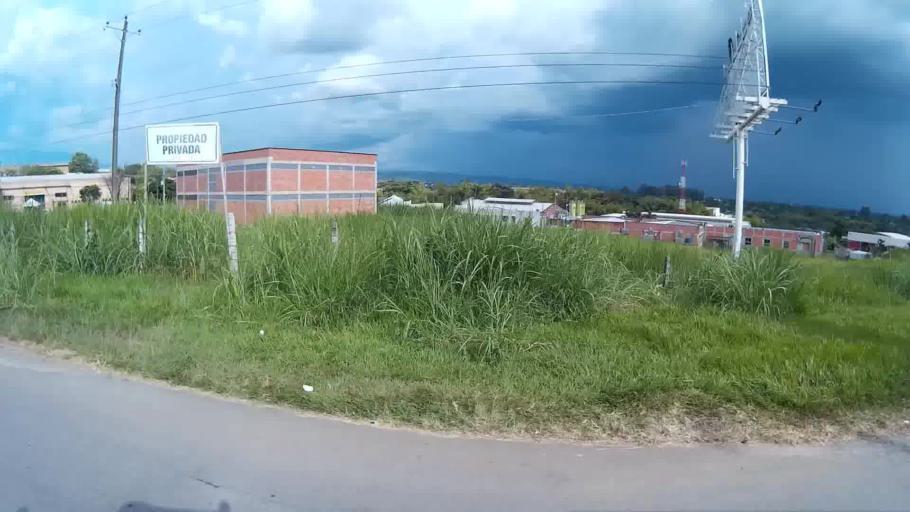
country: CO
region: Risaralda
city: Pereira
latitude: 4.8135
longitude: -75.7651
